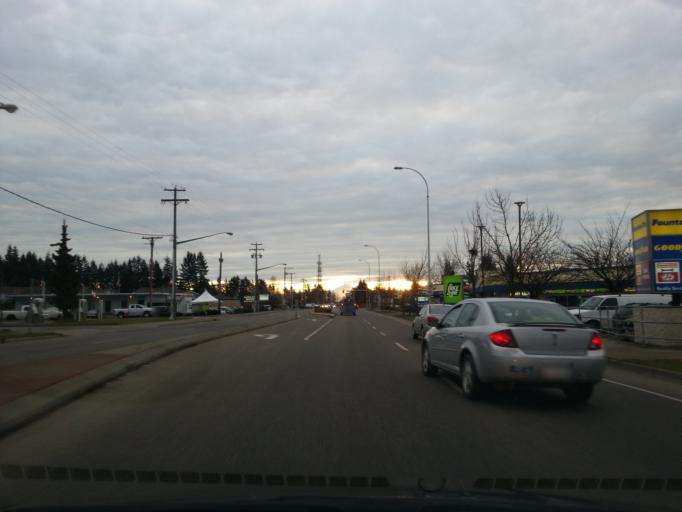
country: CA
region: British Columbia
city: Surrey
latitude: 49.1640
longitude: -122.7962
